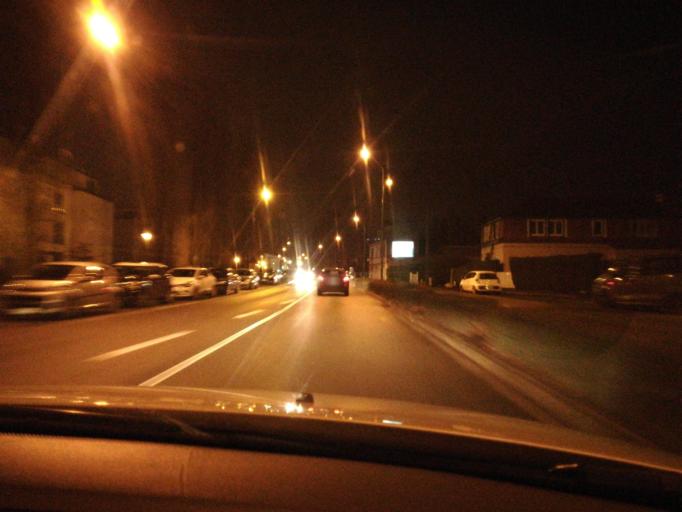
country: FR
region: Haute-Normandie
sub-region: Departement de la Seine-Maritime
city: Bois-Guillaume
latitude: 49.4694
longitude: 1.1257
